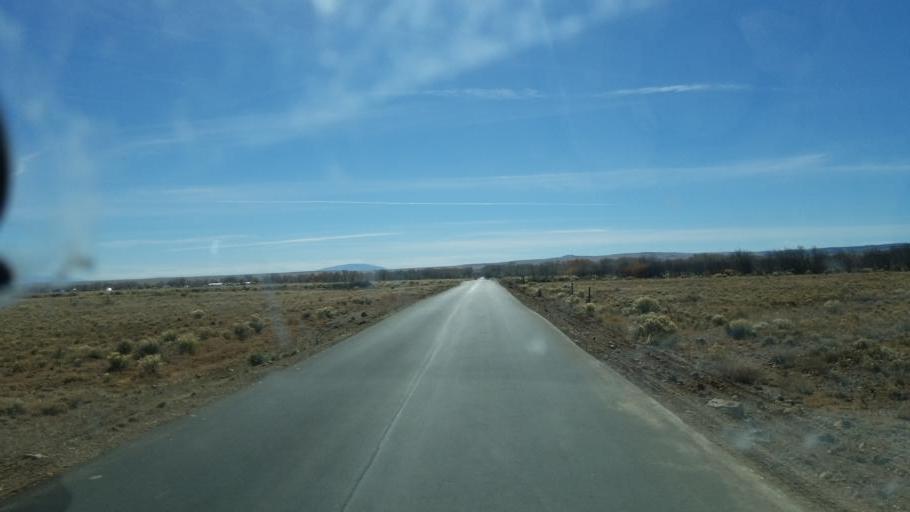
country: US
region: Colorado
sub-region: Conejos County
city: Conejos
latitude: 37.3090
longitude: -106.1484
